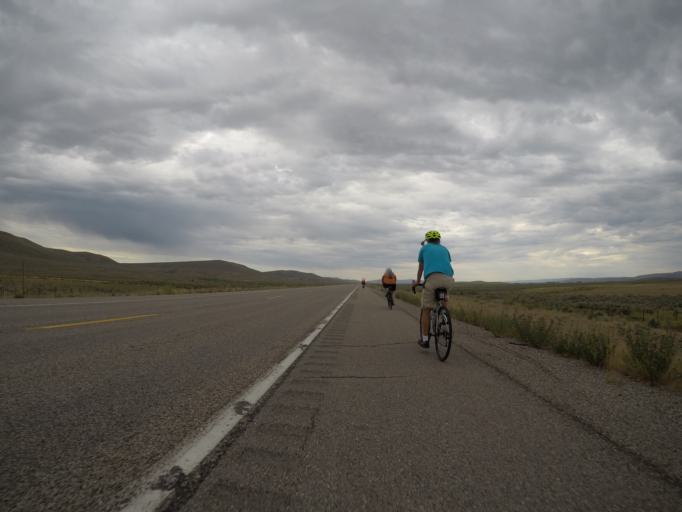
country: US
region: Utah
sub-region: Rich County
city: Randolph
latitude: 41.9035
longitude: -110.9574
